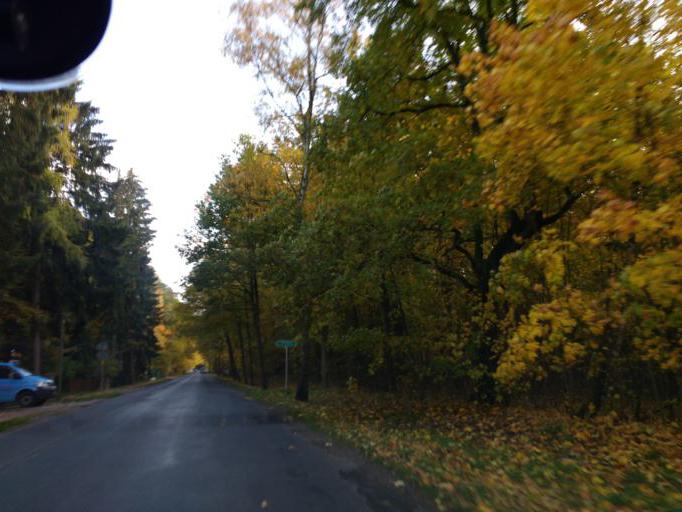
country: DE
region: Brandenburg
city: Petershagen
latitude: 52.5544
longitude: 13.8347
